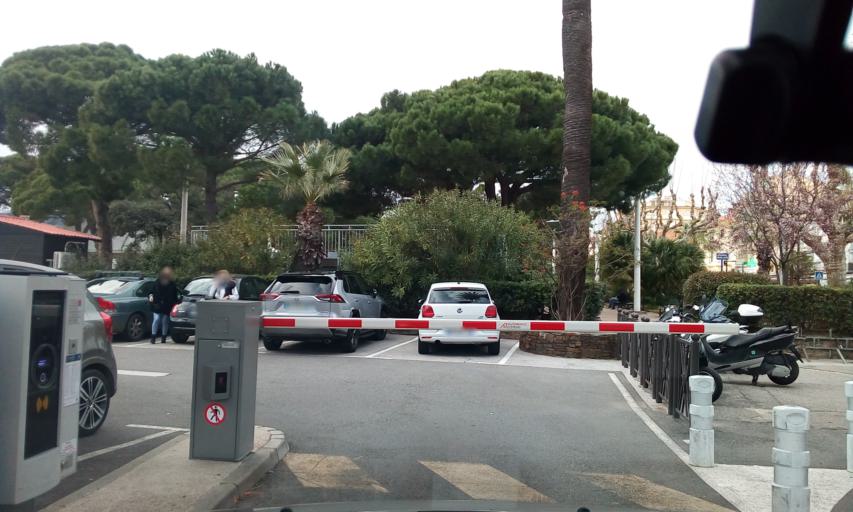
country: FR
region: Provence-Alpes-Cote d'Azur
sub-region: Departement du Var
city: Sainte-Maxime
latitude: 43.3080
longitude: 6.6397
